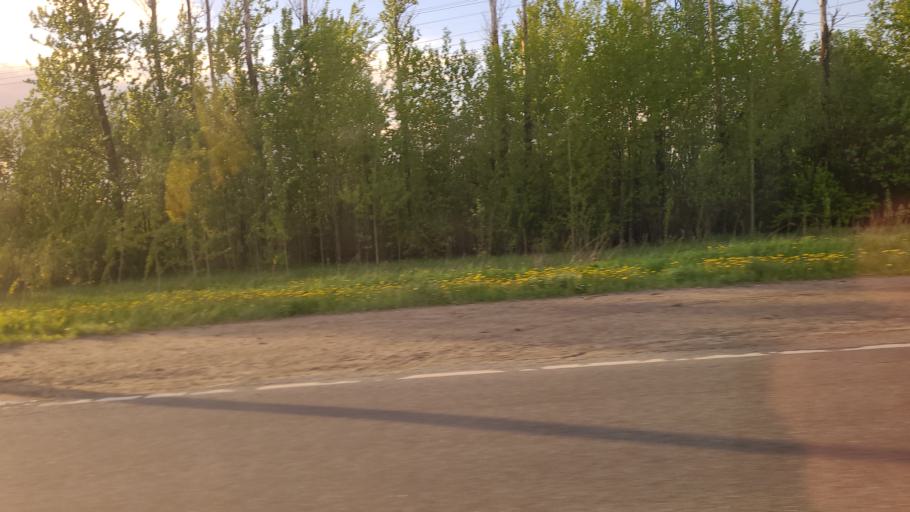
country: RU
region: St.-Petersburg
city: Kolpino
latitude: 59.7490
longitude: 30.5431
